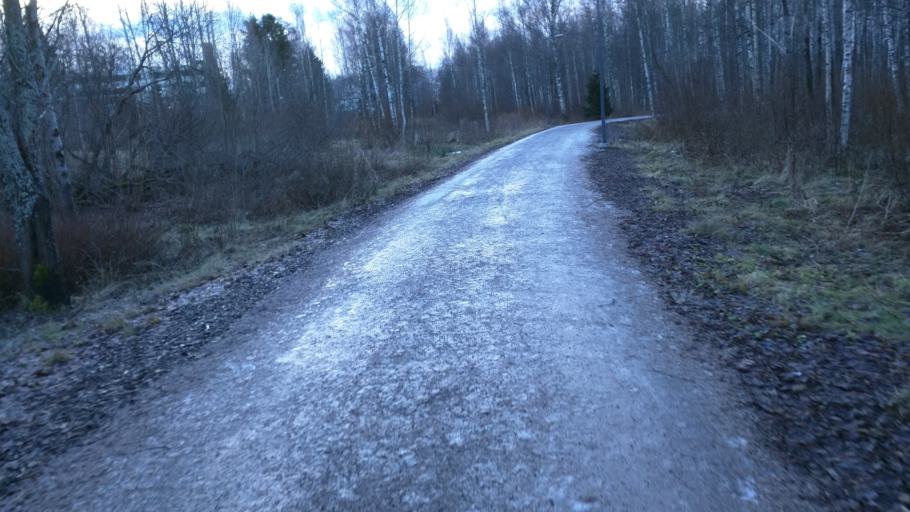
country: FI
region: Uusimaa
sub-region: Helsinki
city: Kauniainen
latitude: 60.2395
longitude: 24.7329
